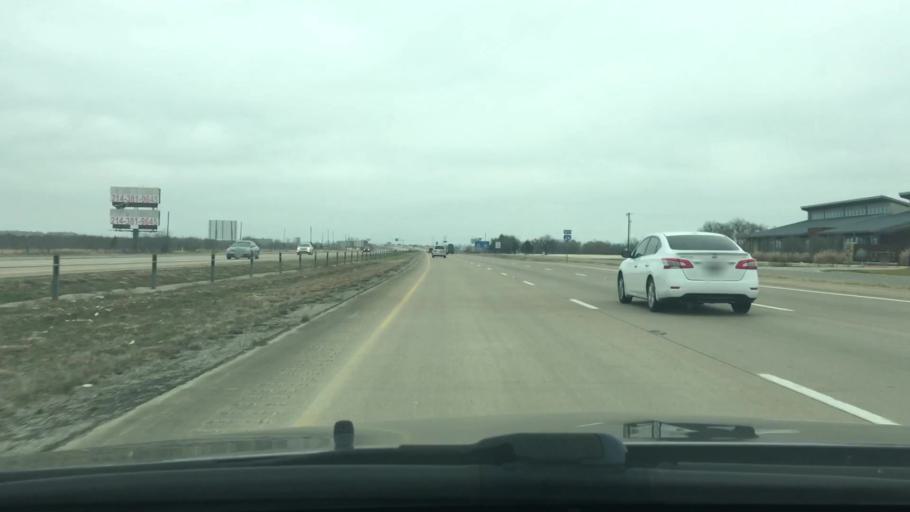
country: US
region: Texas
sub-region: Ellis County
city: Ennis
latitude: 32.3203
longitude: -96.6058
